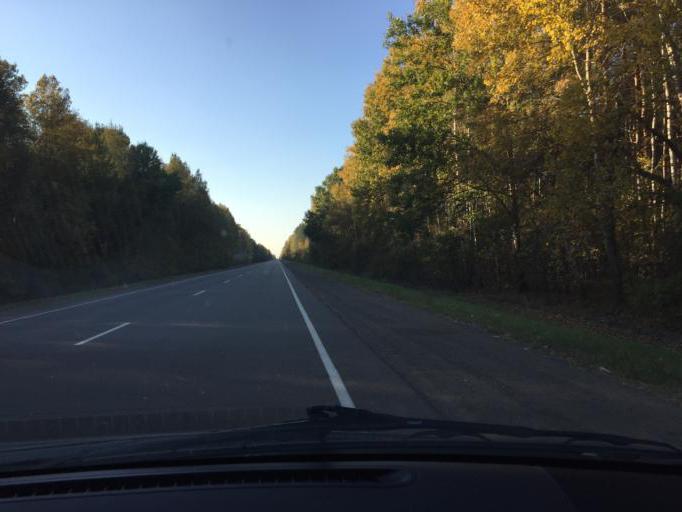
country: BY
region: Brest
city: Horad Luninyets
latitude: 52.2932
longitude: 26.7610
